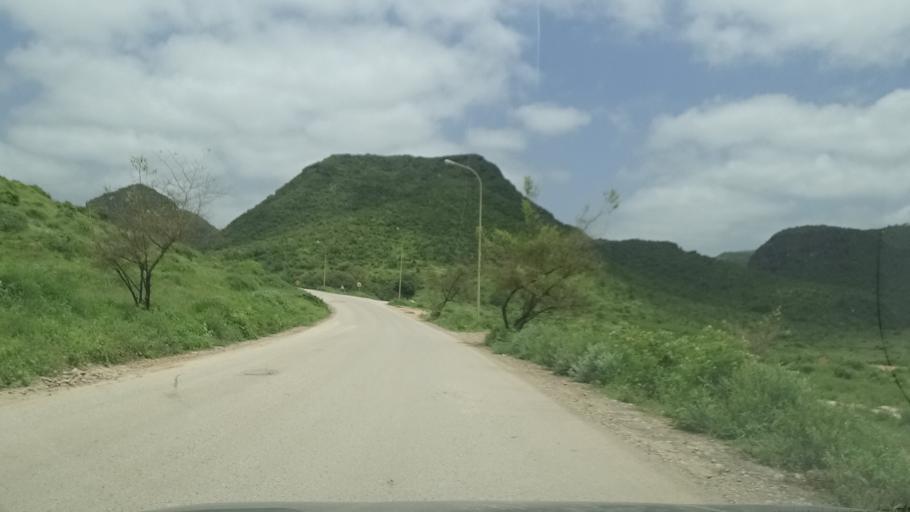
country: OM
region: Zufar
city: Salalah
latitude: 17.1482
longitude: 54.1769
